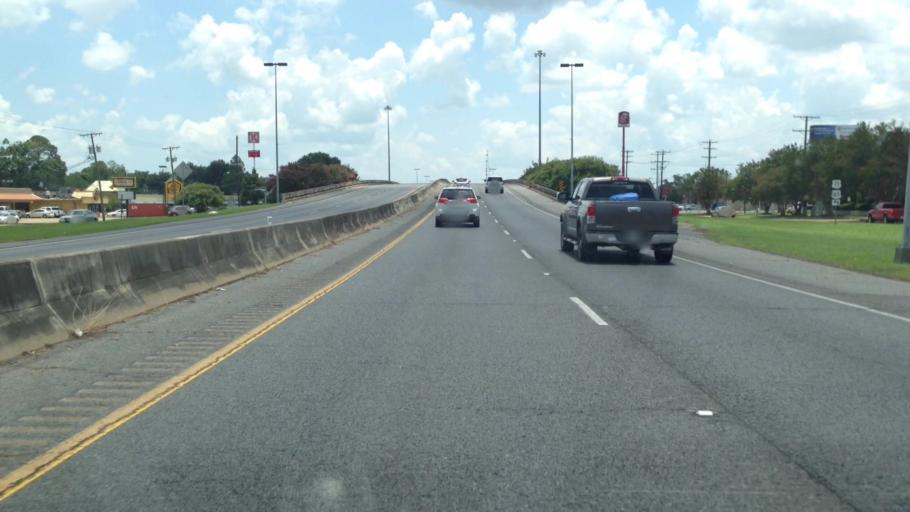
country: US
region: Louisiana
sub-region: Rapides Parish
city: Alexandria
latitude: 31.2883
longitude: -92.4757
